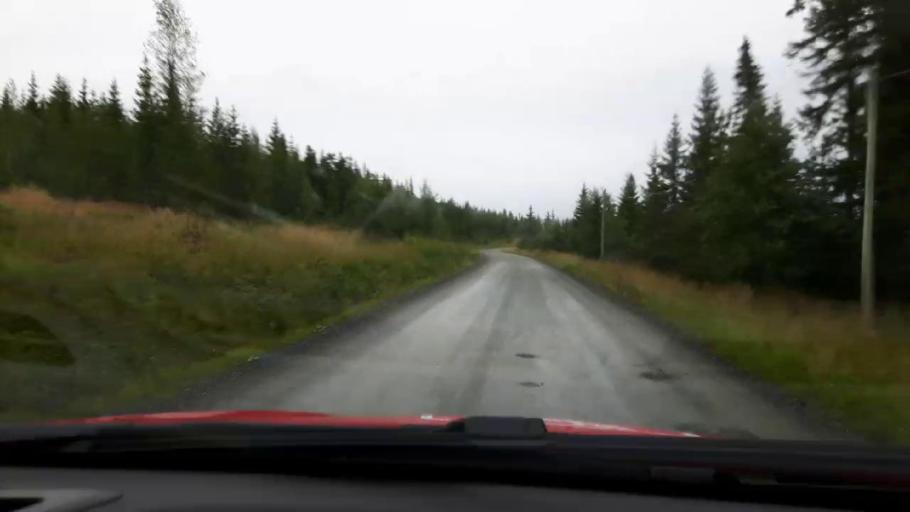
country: SE
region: Jaemtland
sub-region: Are Kommun
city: Are
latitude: 63.4240
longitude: 12.8186
